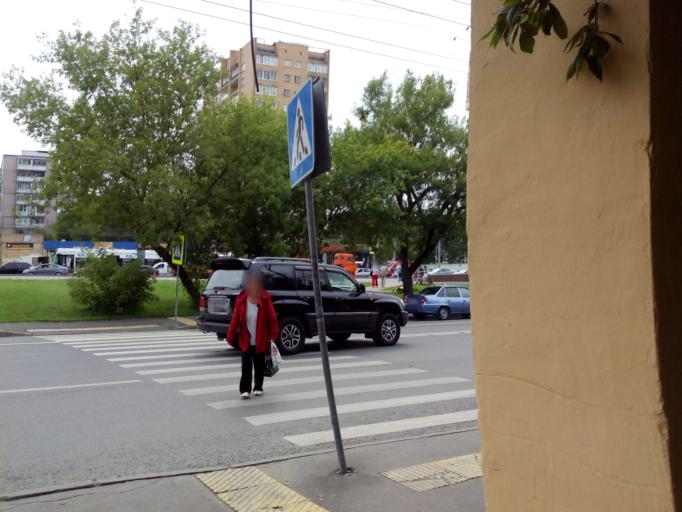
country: RU
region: Moscow
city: Pokrovskoye-Streshnevo
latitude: 55.8174
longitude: 37.4618
